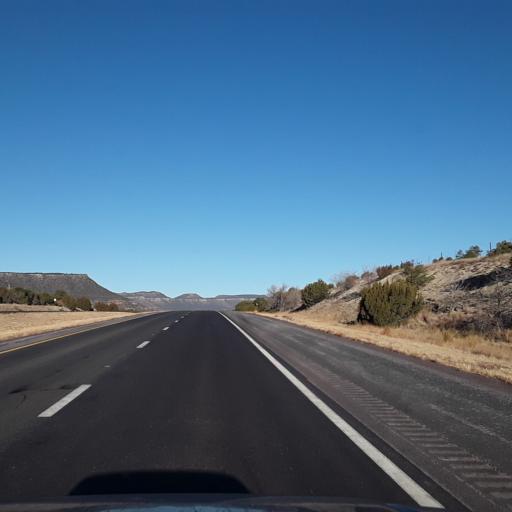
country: US
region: New Mexico
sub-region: San Miguel County
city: Pecos
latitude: 35.4359
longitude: -105.6060
